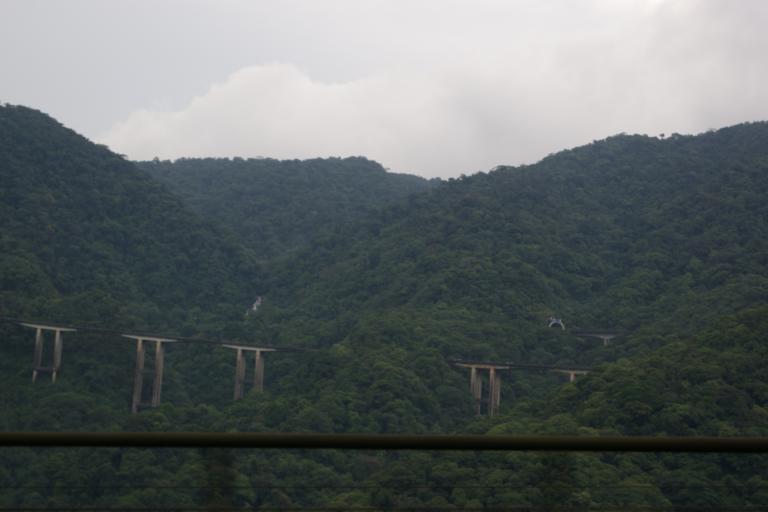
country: BR
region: Sao Paulo
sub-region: Cubatao
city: Cubatao
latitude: -23.8983
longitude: -46.4917
